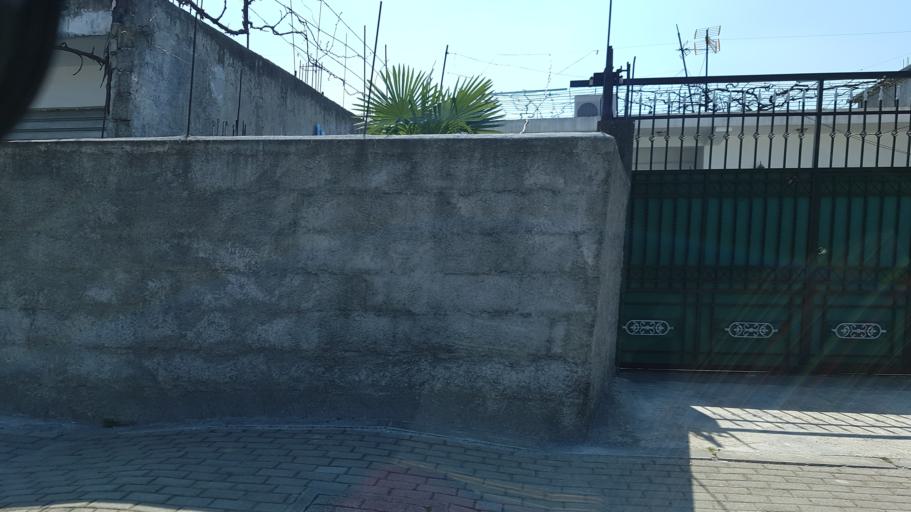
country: AL
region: Shkoder
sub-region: Rrethi i Shkodres
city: Shkoder
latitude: 42.0558
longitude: 19.5168
